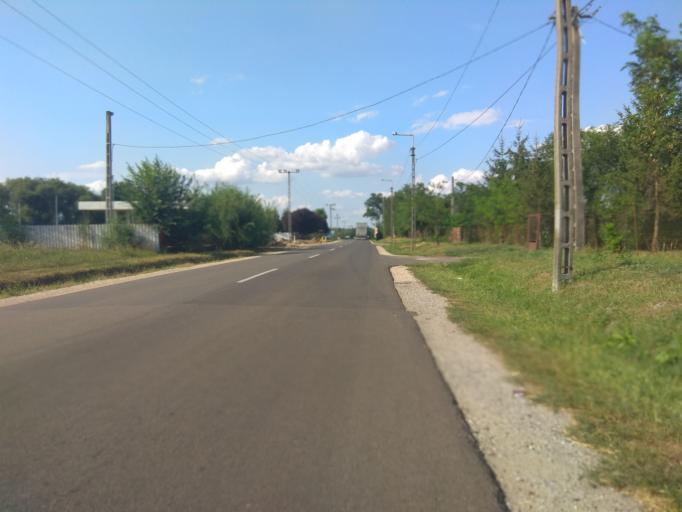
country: HU
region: Borsod-Abauj-Zemplen
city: Mezocsat
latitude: 47.8346
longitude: 20.9004
